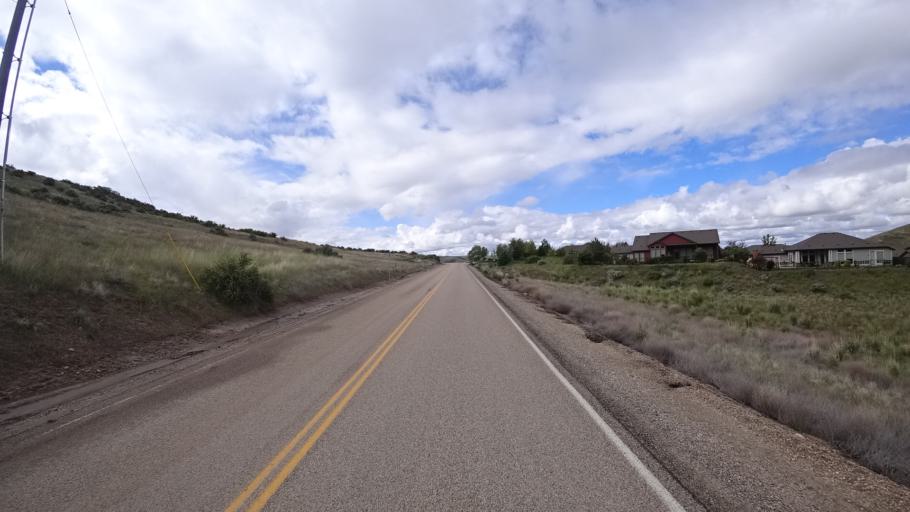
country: US
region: Idaho
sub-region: Ada County
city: Garden City
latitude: 43.7251
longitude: -116.2347
